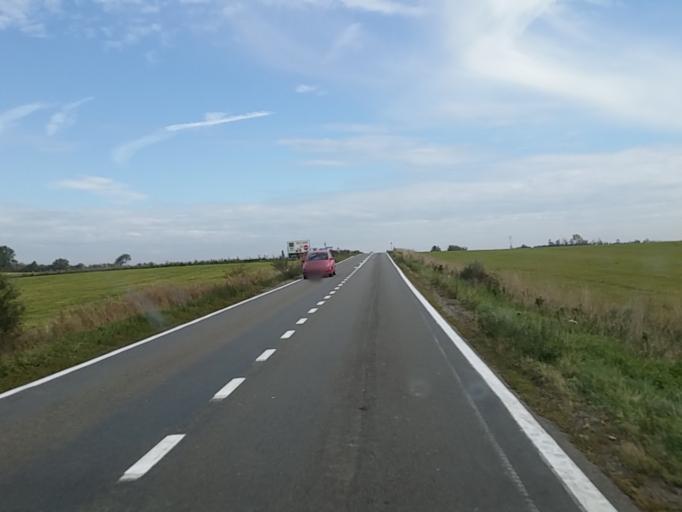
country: BE
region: Wallonia
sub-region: Province du Luxembourg
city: Habay-la-Vieille
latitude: 49.6983
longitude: 5.6187
